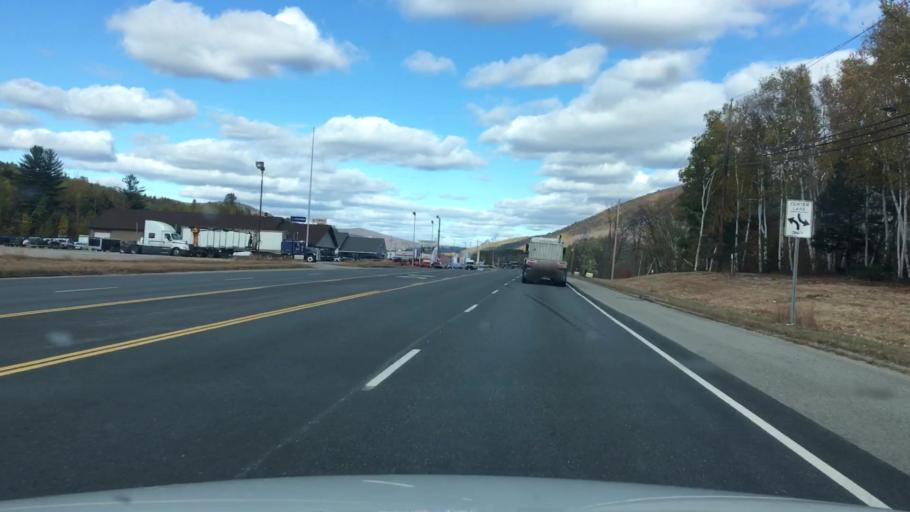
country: US
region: New Hampshire
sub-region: Coos County
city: Gorham
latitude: 44.4085
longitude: -71.1967
